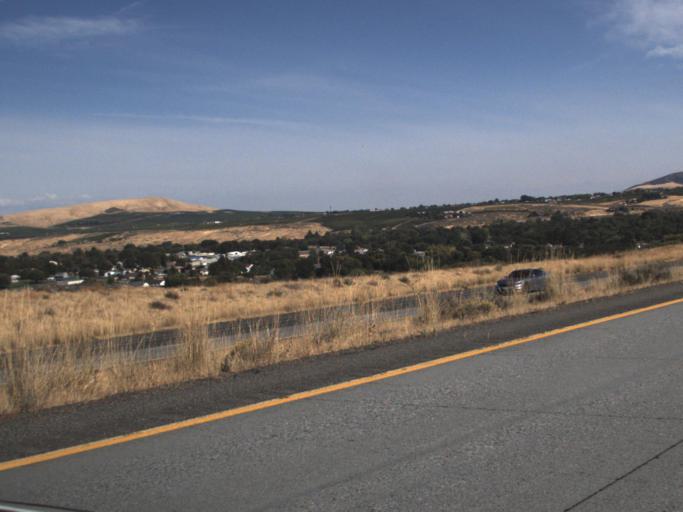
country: US
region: Washington
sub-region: Benton County
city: Benton City
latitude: 46.2578
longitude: -119.5057
